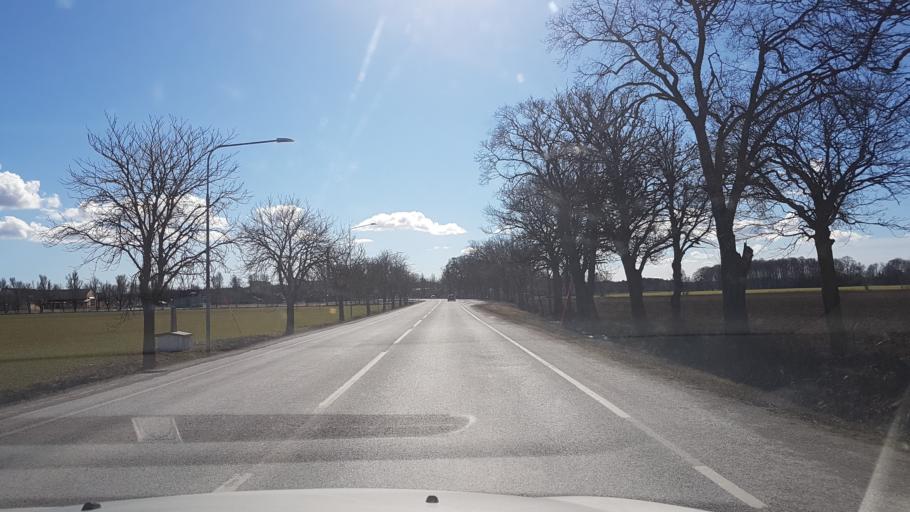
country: SE
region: Gotland
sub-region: Gotland
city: Visby
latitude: 57.5138
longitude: 18.4451
